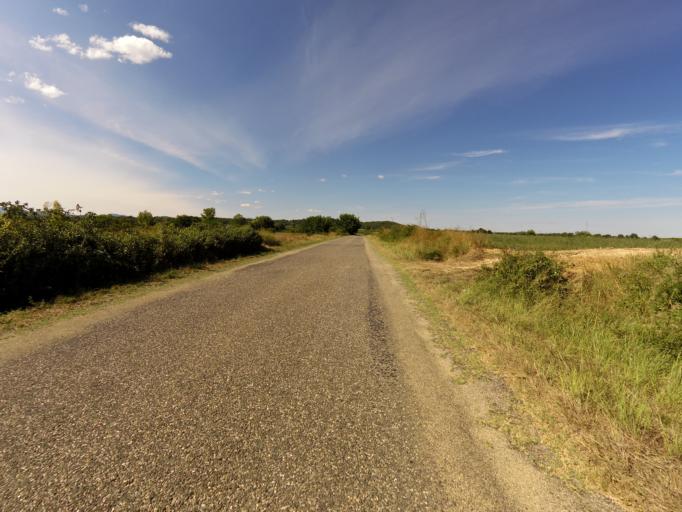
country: FR
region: Languedoc-Roussillon
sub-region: Departement du Gard
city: Quissac
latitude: 43.9635
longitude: 4.0259
